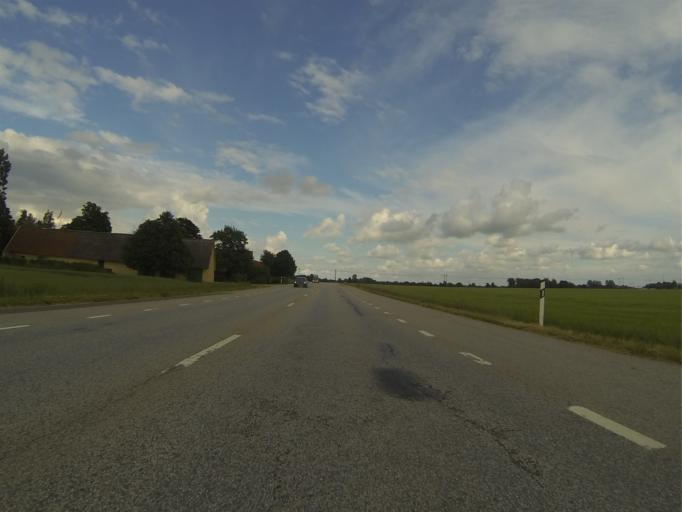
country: SE
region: Skane
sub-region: Staffanstorps Kommun
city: Staffanstorp
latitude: 55.6399
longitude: 13.1723
